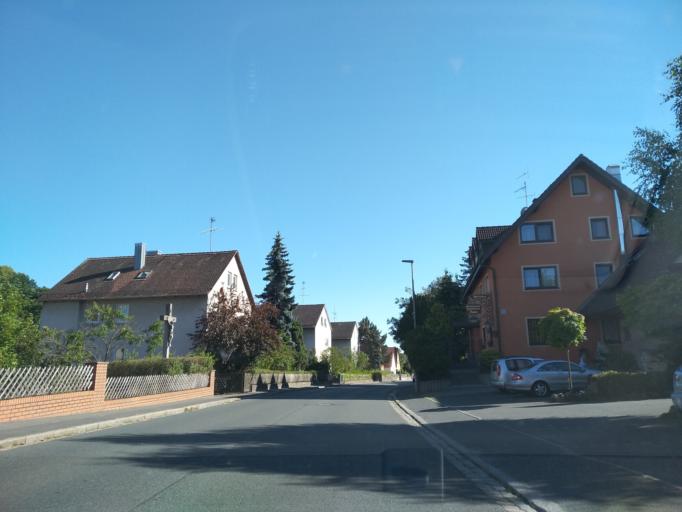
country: DE
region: Bavaria
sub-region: Regierungsbezirk Mittelfranken
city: Rottenbach
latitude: 49.6669
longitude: 10.9241
